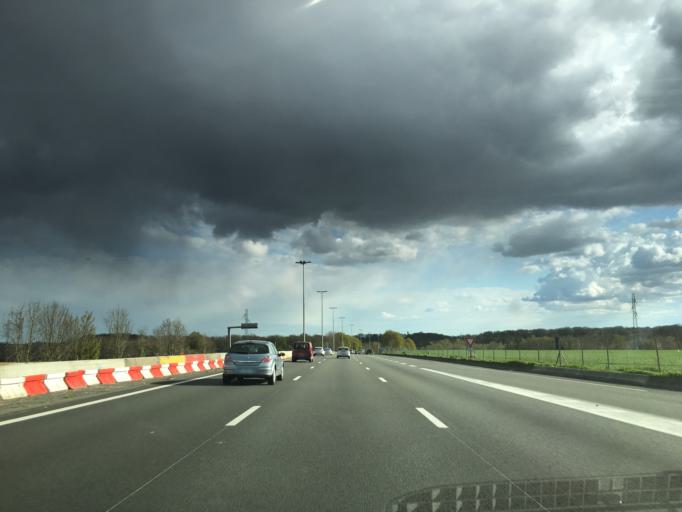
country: FR
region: Ile-de-France
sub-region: Departement du Val-d'Oise
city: Vemars
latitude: 49.0689
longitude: 2.5524
